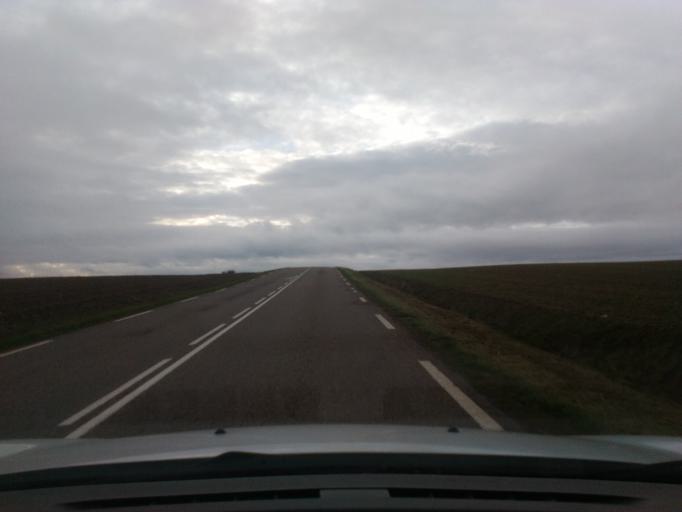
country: FR
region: Lorraine
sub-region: Departement des Vosges
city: Rambervillers
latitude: 48.3541
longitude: 6.6015
